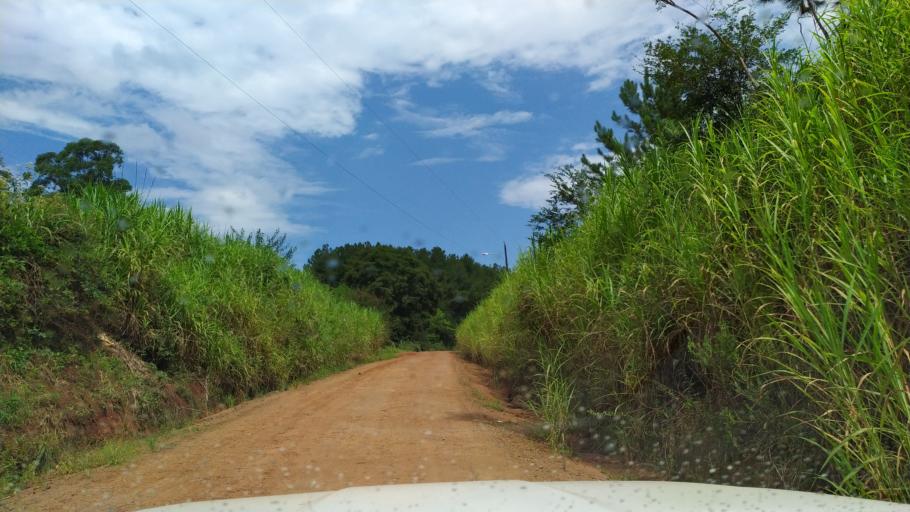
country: AR
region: Misiones
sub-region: Departamento de Eldorado
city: Eldorado
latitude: -26.4937
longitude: -54.5864
